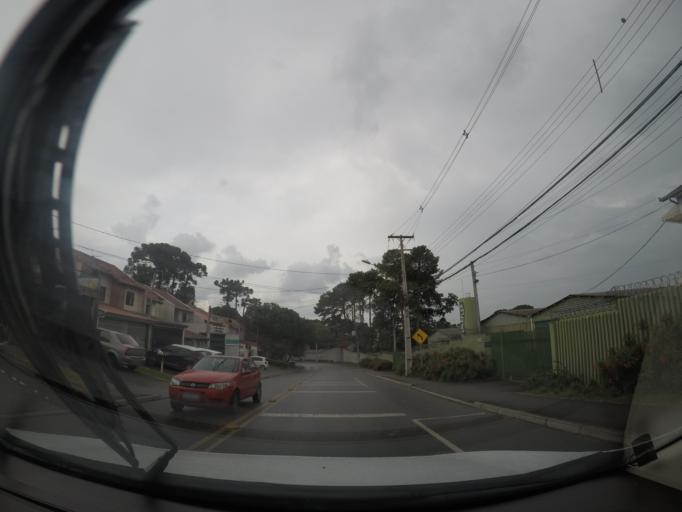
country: BR
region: Parana
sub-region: Sao Jose Dos Pinhais
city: Sao Jose dos Pinhais
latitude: -25.5178
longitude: -49.2526
